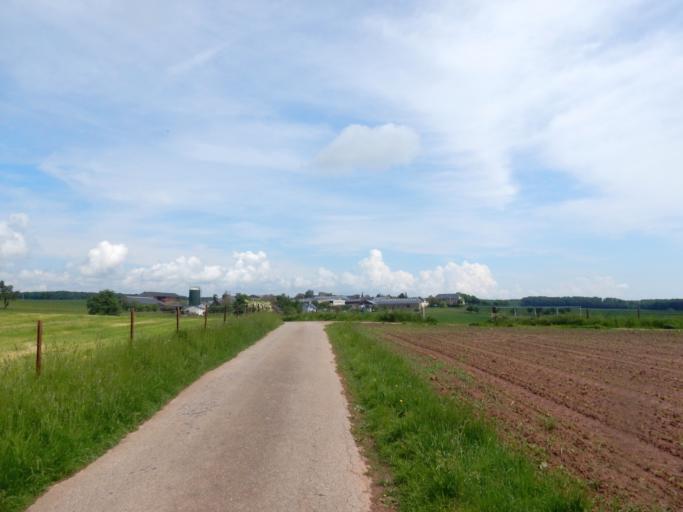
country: LU
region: Diekirch
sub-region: Canton de Redange
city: Vichten
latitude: 49.8139
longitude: 6.0145
